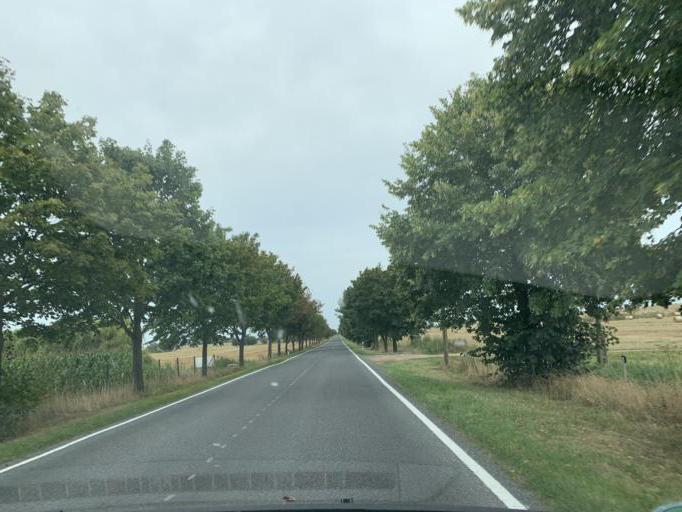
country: DE
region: Brandenburg
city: Gransee
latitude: 53.0022
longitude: 13.1843
